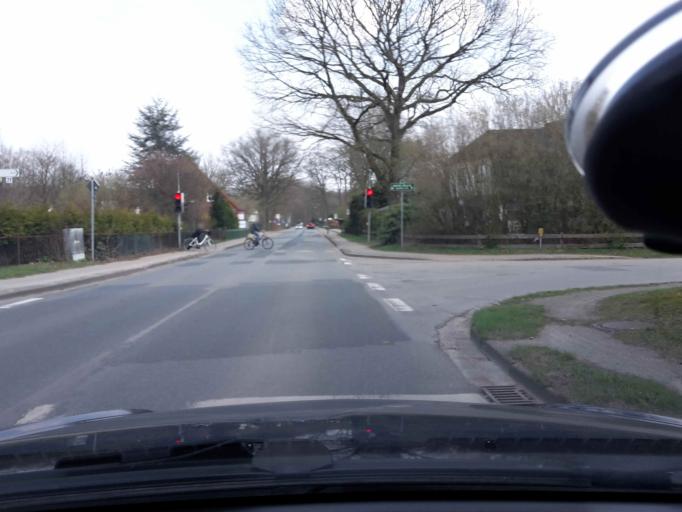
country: DE
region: Lower Saxony
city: Buchholz in der Nordheide
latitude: 53.3000
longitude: 9.8745
